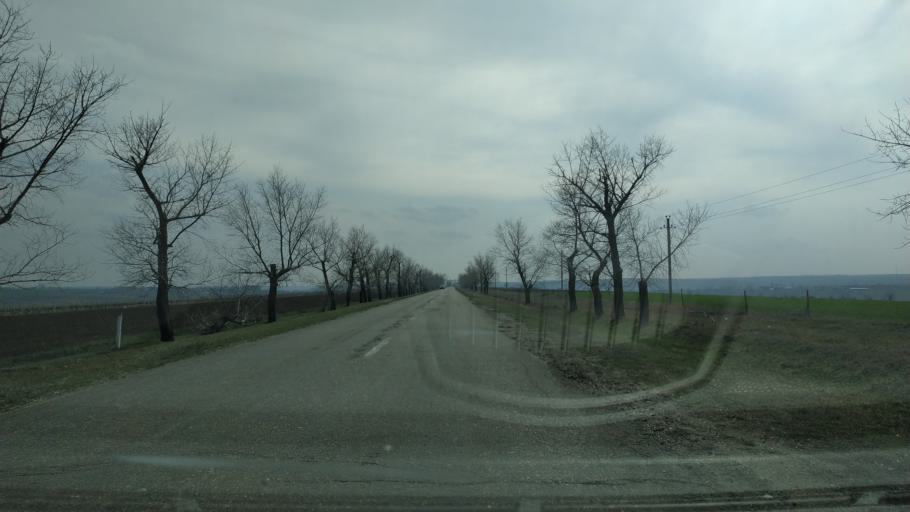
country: MD
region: Gagauzia
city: Vulcanesti
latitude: 45.7125
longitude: 28.4001
